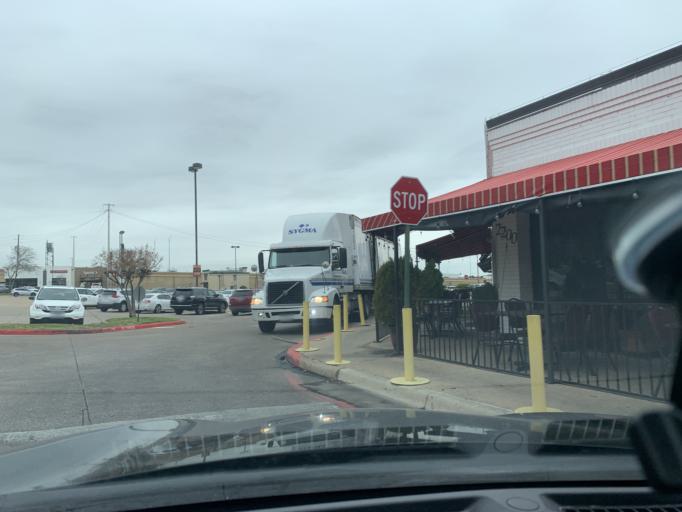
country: US
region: Texas
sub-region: Tarrant County
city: Bedford
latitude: 32.8348
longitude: -97.1328
